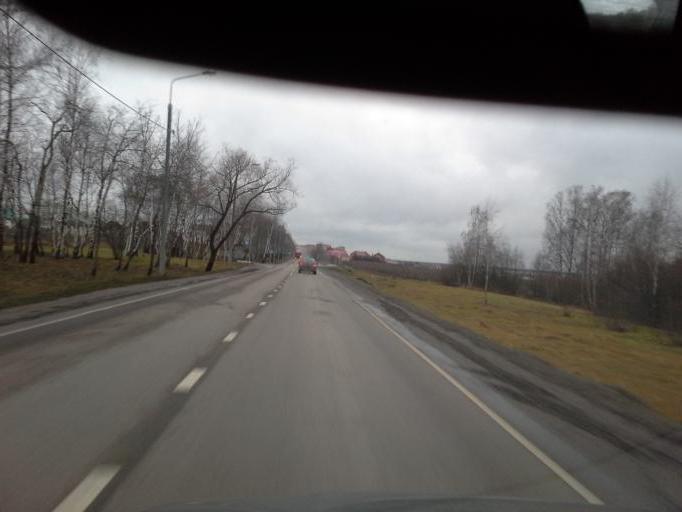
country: RU
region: Moscow
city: Vnukovo
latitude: 55.5938
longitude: 37.2272
